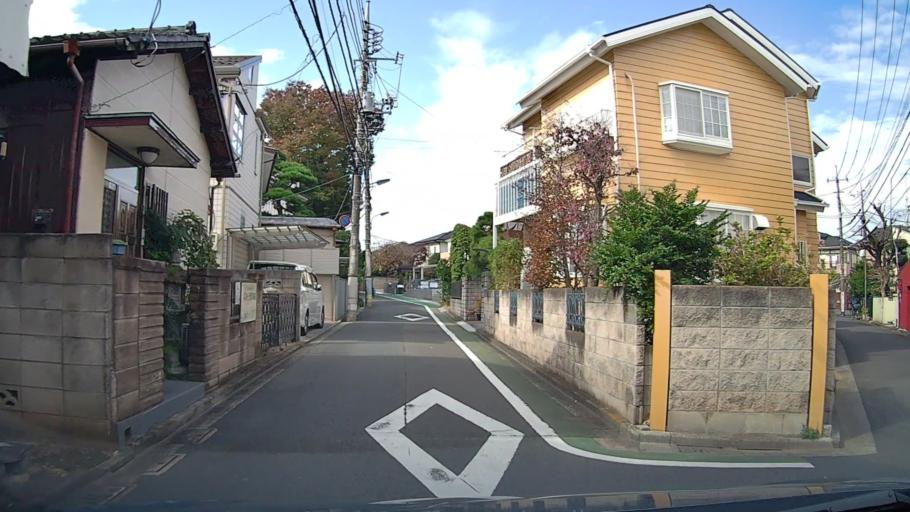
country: JP
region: Saitama
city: Wako
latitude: 35.7363
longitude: 139.6135
